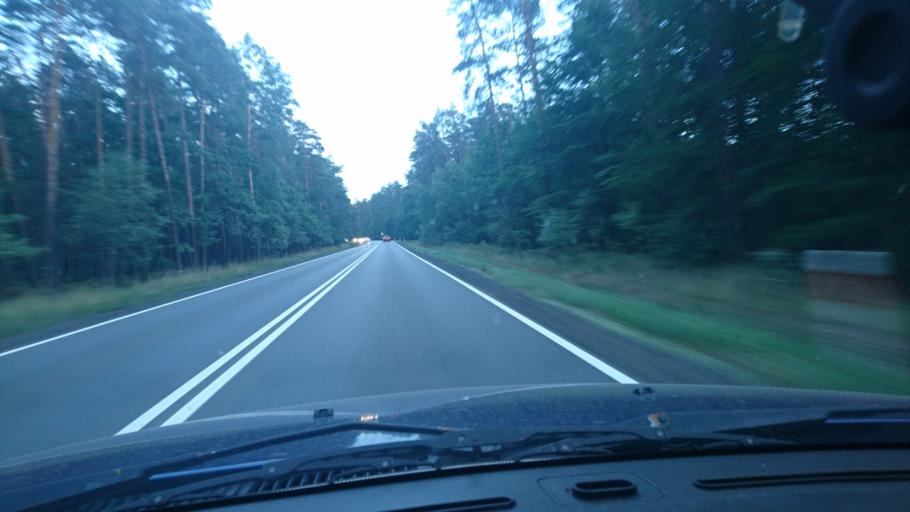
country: PL
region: Silesian Voivodeship
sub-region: Powiat tarnogorski
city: Tworog
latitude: 50.4952
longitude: 18.7728
